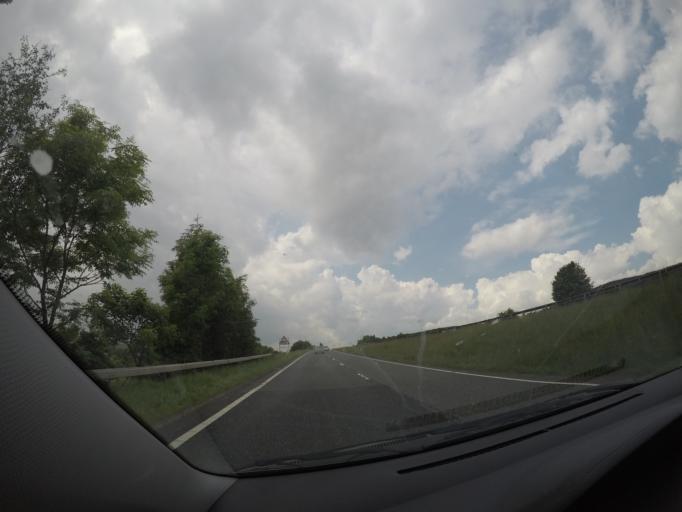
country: GB
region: England
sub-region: County Durham
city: Bowes
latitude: 54.5139
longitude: -2.0408
